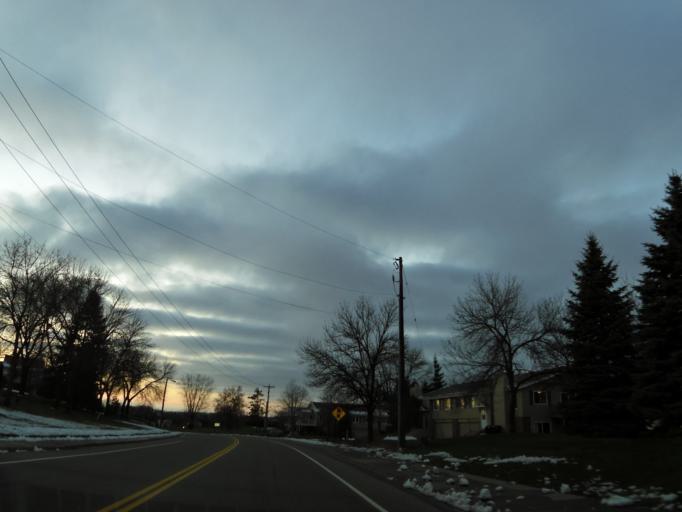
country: US
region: Minnesota
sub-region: Hennepin County
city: Minnetonka Mills
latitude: 44.9063
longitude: -93.4252
